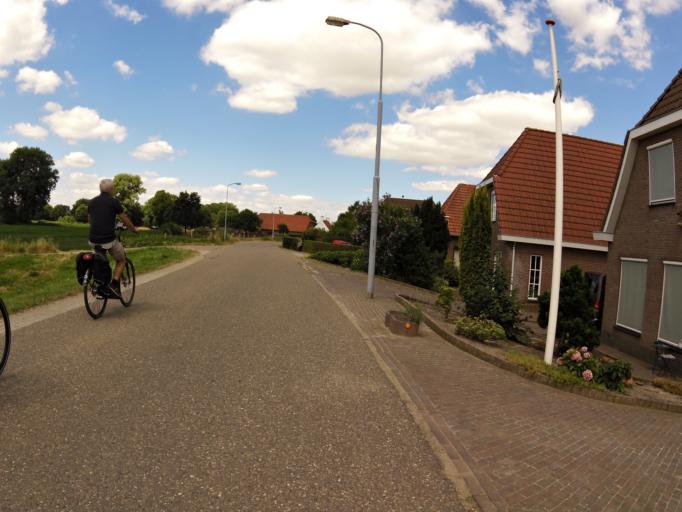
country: NL
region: Gelderland
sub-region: Gemeente Maasdriel
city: Heerewaarden
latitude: 51.7857
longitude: 5.3424
